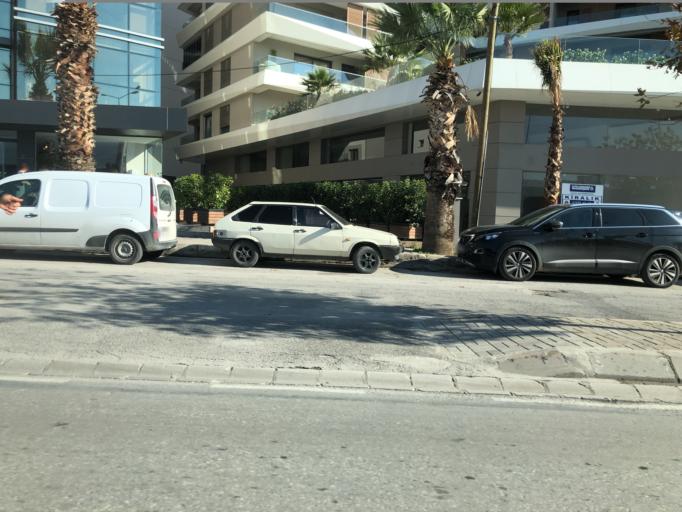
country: TR
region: Izmir
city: Izmir
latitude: 38.4580
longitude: 27.1753
